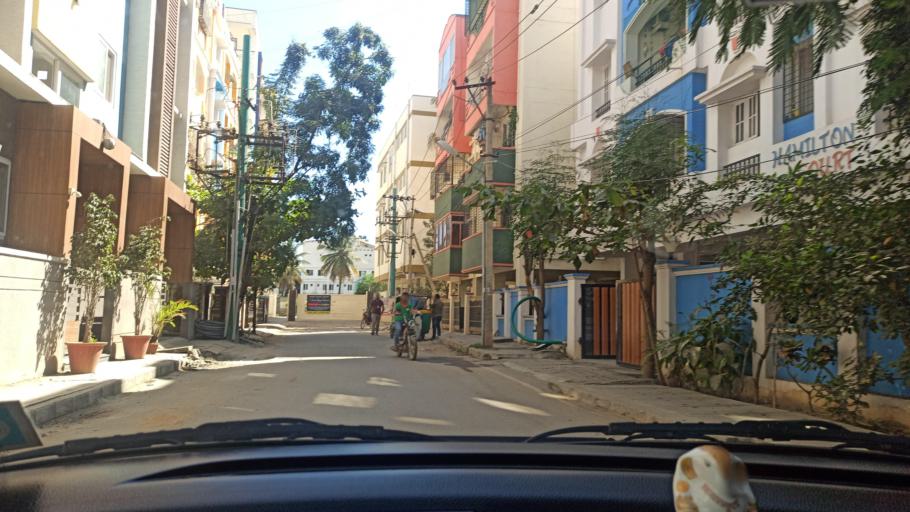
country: IN
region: Karnataka
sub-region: Bangalore Urban
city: Bangalore
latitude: 12.9252
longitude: 77.6713
